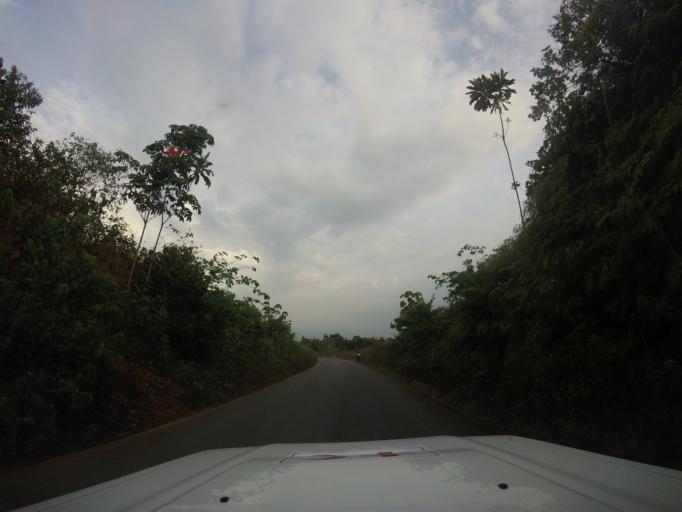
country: LR
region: Bomi
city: Tubmanburg
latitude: 6.7038
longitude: -10.9220
